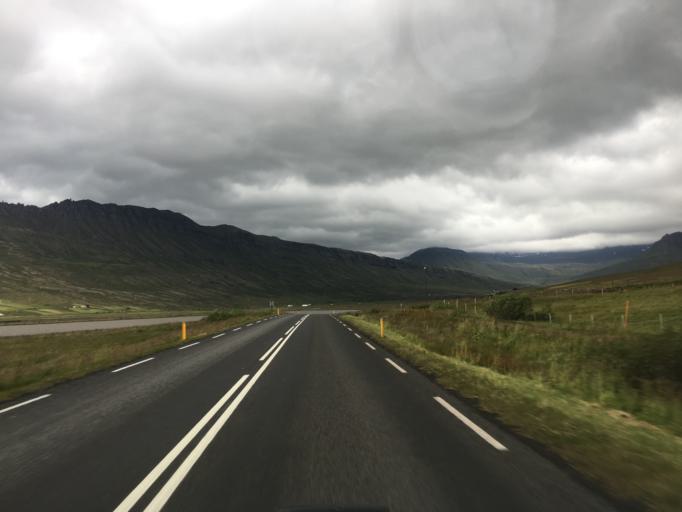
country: IS
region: East
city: Neskaupstadur
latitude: 65.1362
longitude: -13.7488
